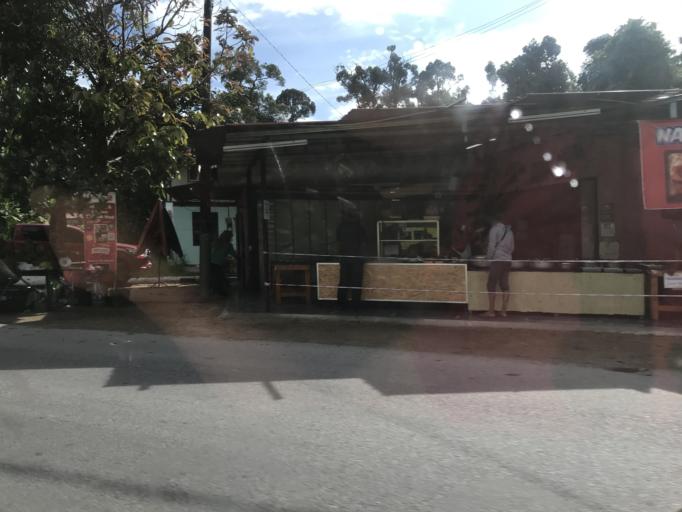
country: MY
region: Kelantan
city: Kota Bharu
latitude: 6.1225
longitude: 102.1753
